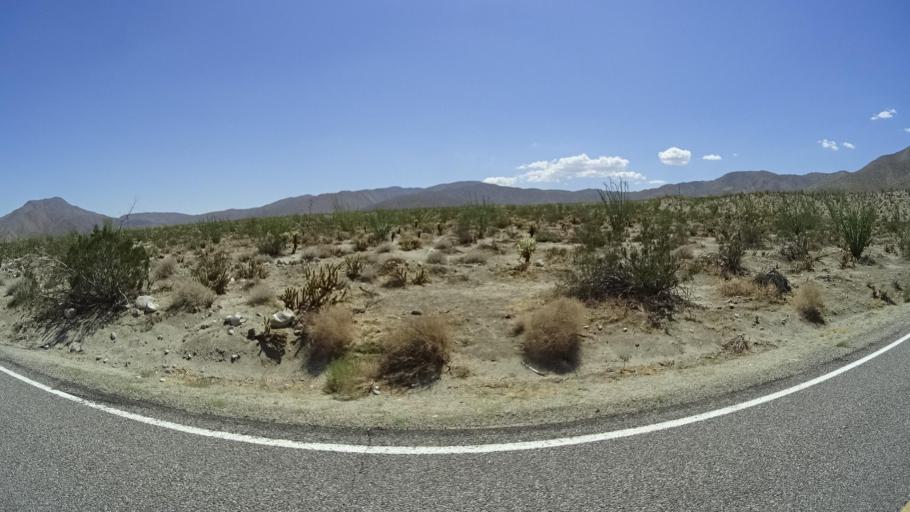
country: US
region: California
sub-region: San Diego County
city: Borrego Springs
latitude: 33.1355
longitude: -116.3546
